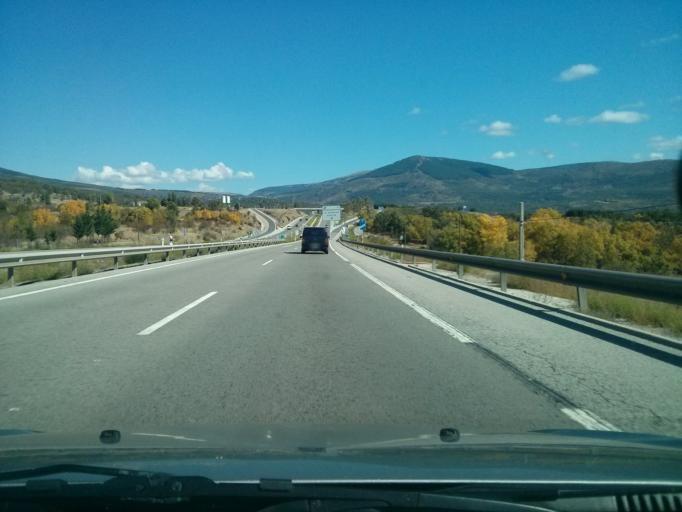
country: ES
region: Madrid
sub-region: Provincia de Madrid
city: Horcajo de la Sierra
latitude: 41.0569
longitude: -3.6130
